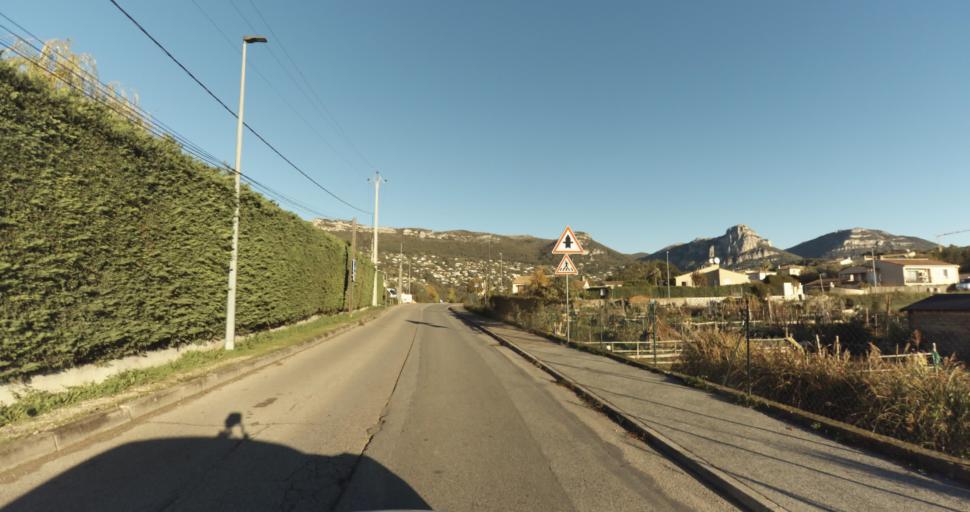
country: FR
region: Provence-Alpes-Cote d'Azur
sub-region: Departement des Alpes-Maritimes
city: Vence
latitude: 43.7170
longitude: 7.1298
